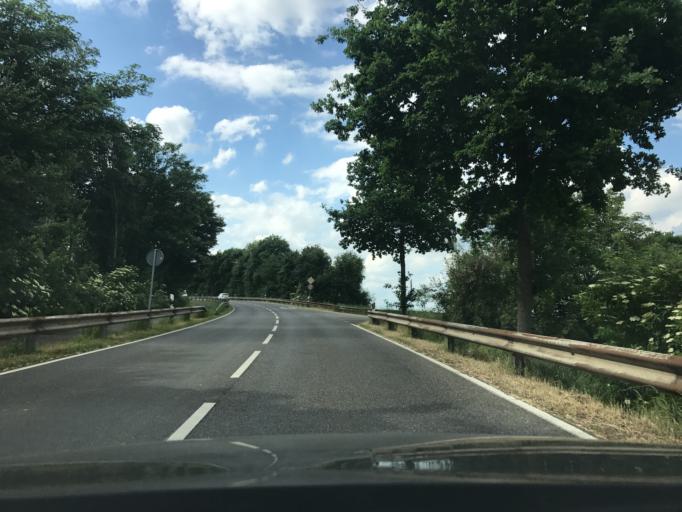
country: DE
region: North Rhine-Westphalia
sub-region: Regierungsbezirk Dusseldorf
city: Krefeld
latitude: 51.3119
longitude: 6.6352
